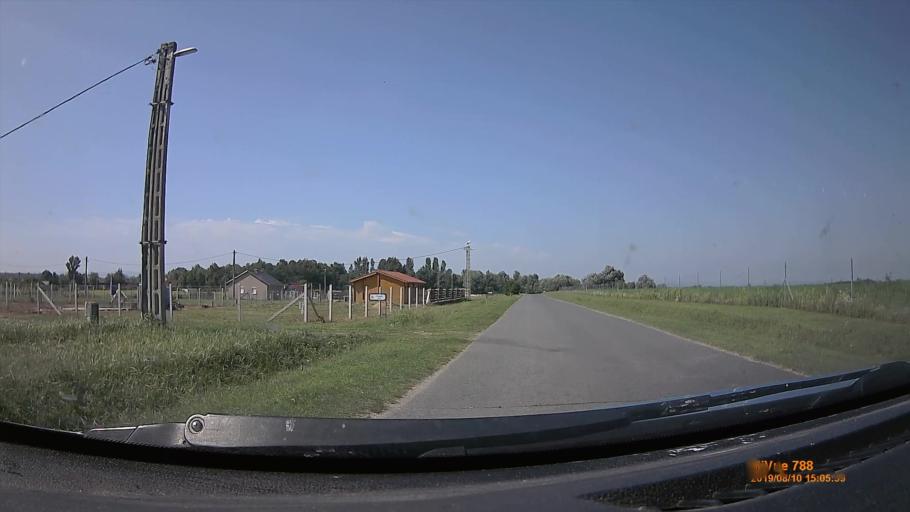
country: HU
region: Somogy
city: Fonyod
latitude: 46.6808
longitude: 17.5646
